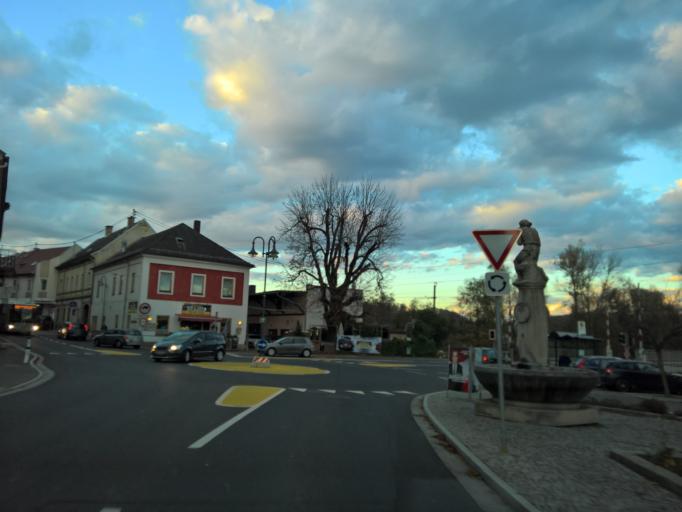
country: AT
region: Styria
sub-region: Politischer Bezirk Leibnitz
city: Wildon
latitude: 46.8859
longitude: 15.5182
